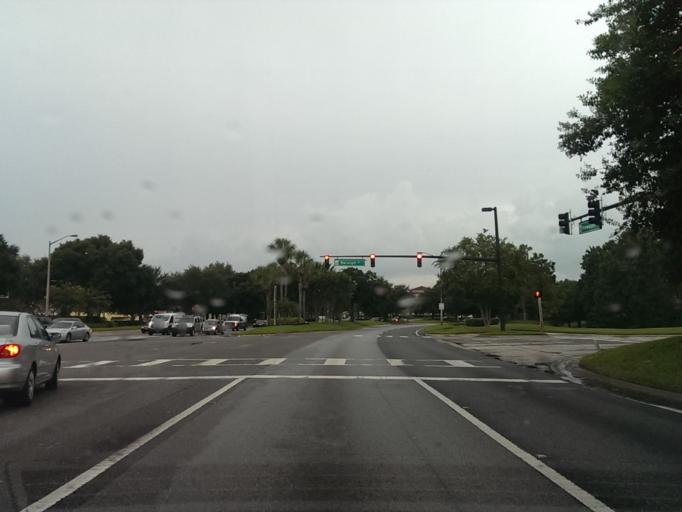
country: US
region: Florida
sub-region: Orange County
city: Orlovista
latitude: 28.5262
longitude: -81.4722
